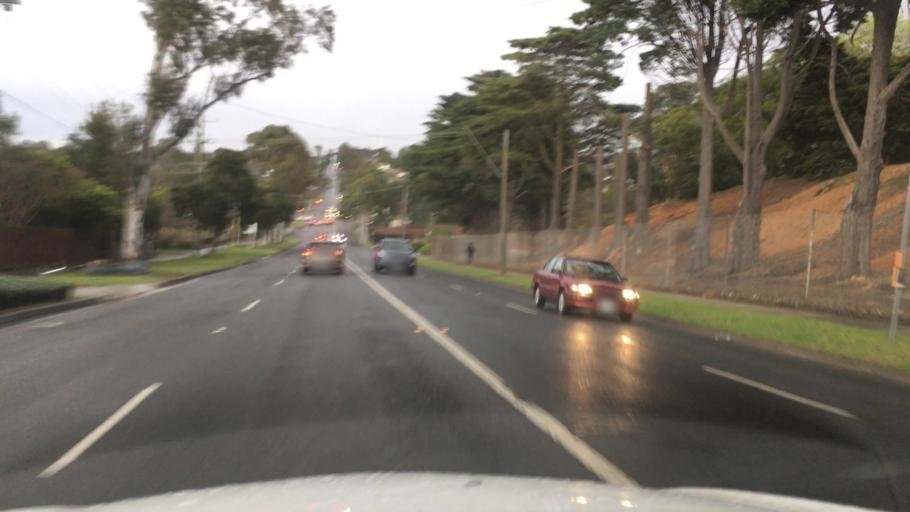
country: AU
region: Victoria
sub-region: Monash
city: Ashwood
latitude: -37.8706
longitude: 145.1112
